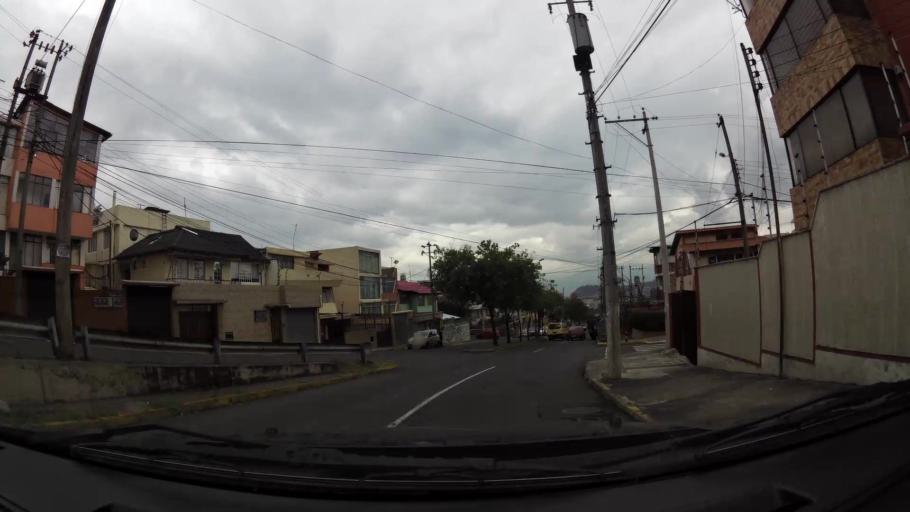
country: EC
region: Pichincha
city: Quito
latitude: -0.1944
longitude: -78.5111
